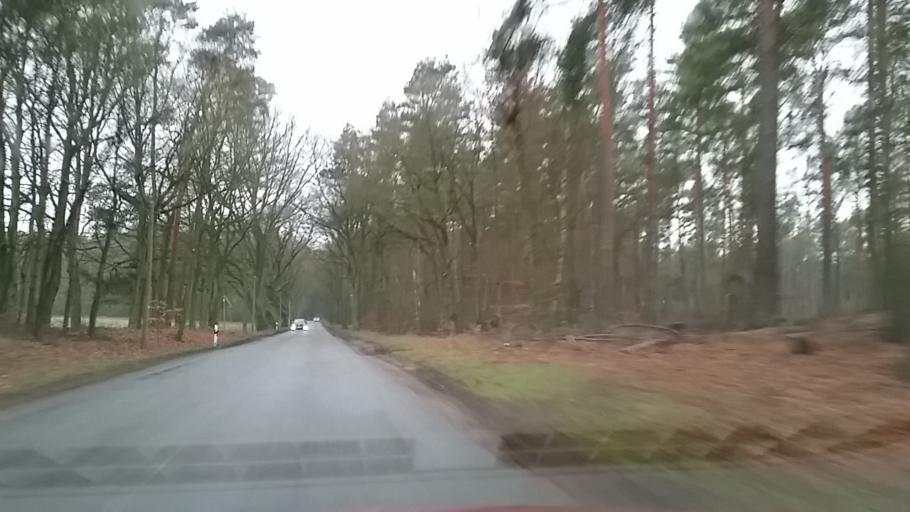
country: DE
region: Brandenburg
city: Gumtow
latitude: 53.0354
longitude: 12.2573
